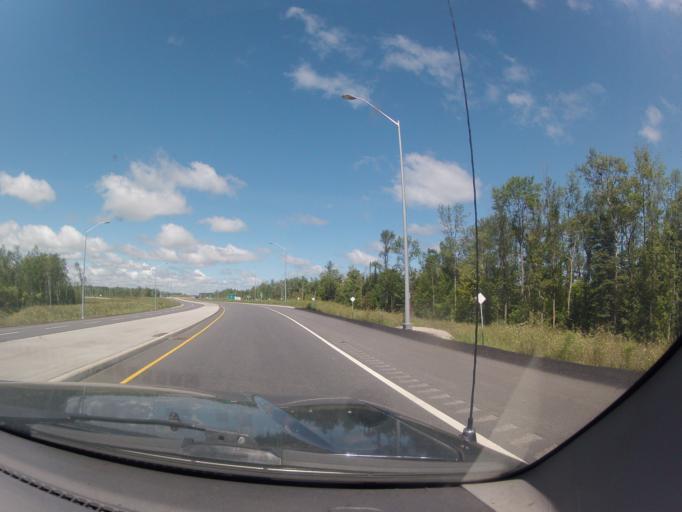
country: CA
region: Ontario
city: Wasaga Beach
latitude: 44.4607
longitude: -80.1087
